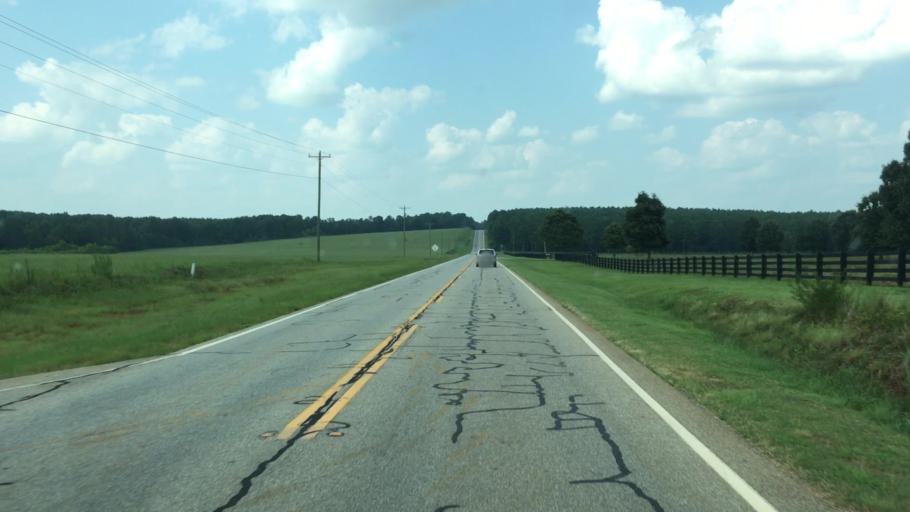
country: US
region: Georgia
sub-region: Jasper County
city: Monticello
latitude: 33.2463
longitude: -83.7215
